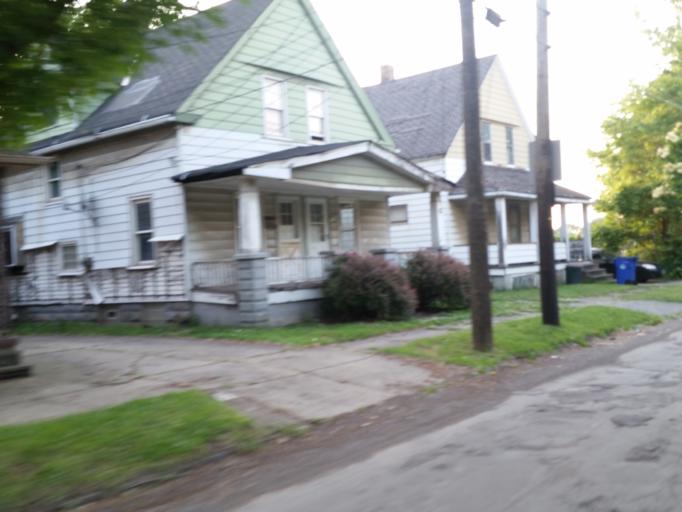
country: US
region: Ohio
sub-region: Cuyahoga County
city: Newburgh Heights
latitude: 41.4599
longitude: -81.6532
